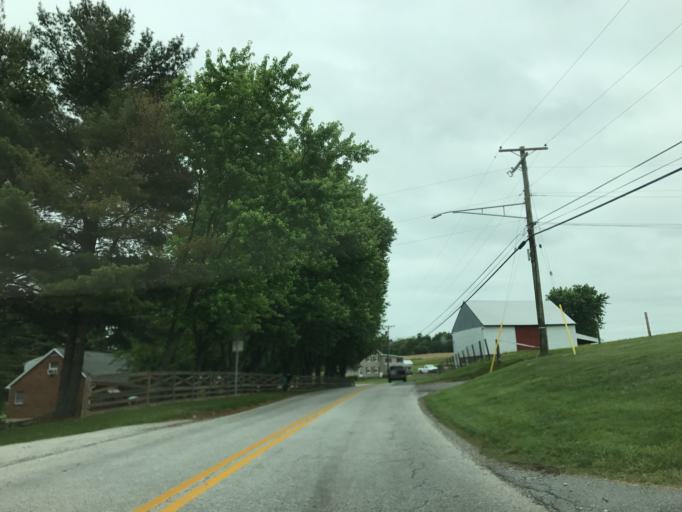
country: US
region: Maryland
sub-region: Carroll County
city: Hampstead
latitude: 39.6384
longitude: -76.8130
